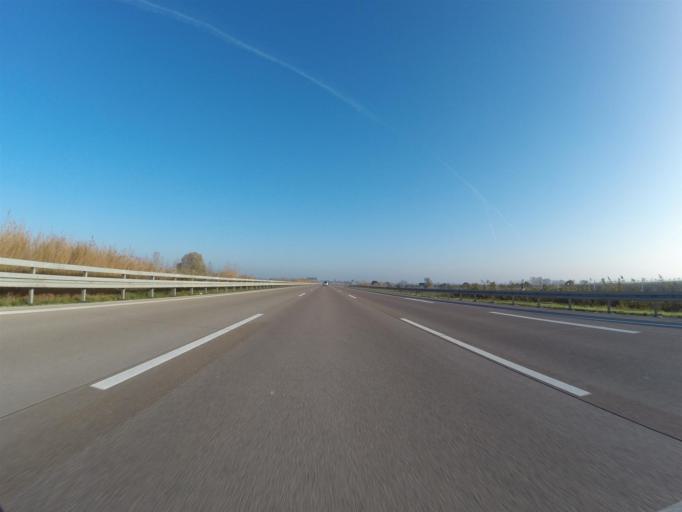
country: DE
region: Saxony-Anhalt
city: Grosskorbetha
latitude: 51.2436
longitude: 12.0659
